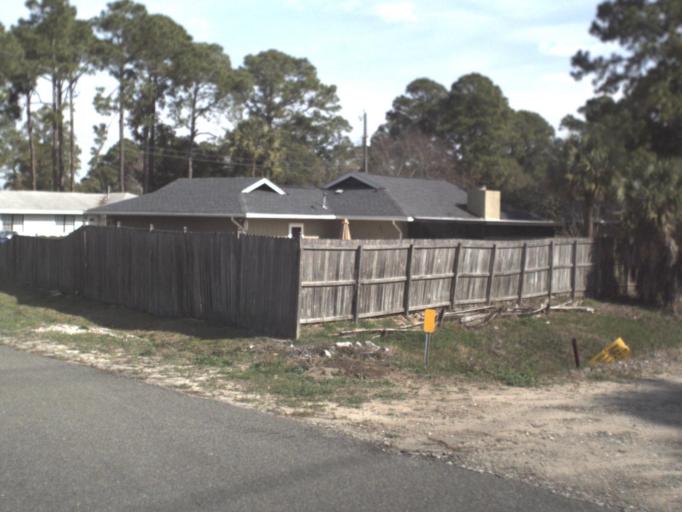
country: US
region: Florida
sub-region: Bay County
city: Pretty Bayou
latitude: 30.1854
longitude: -85.7013
